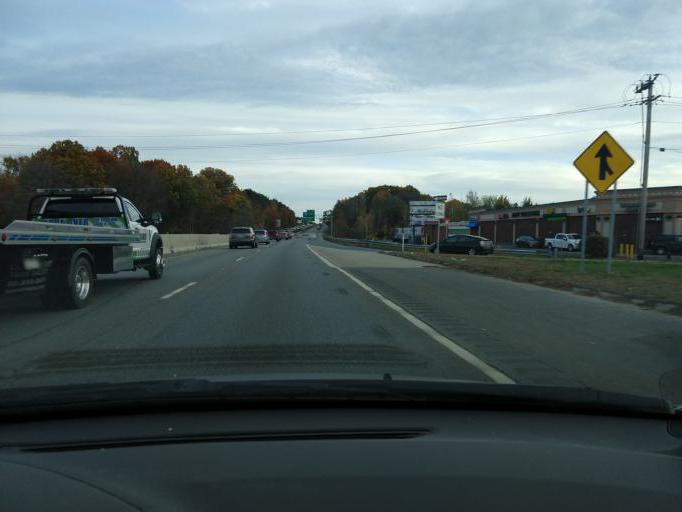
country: US
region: Massachusetts
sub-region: Worcester County
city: Leominster
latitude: 42.5359
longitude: -71.7417
